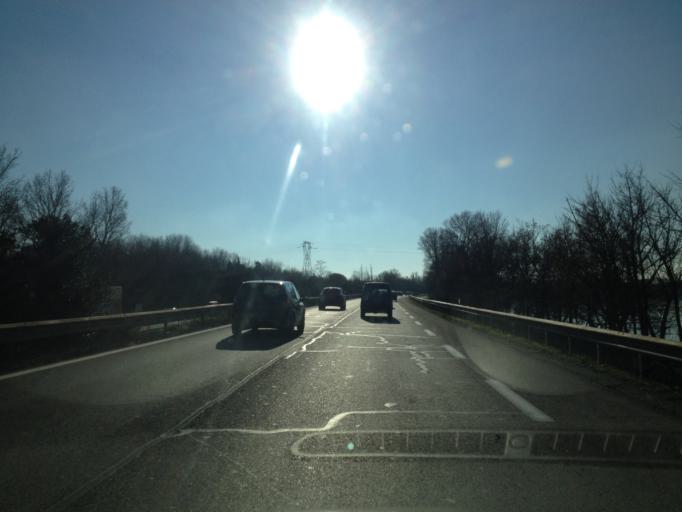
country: FR
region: Provence-Alpes-Cote d'Azur
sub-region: Departement du Vaucluse
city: Le Pontet
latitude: 43.9626
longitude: 4.8502
